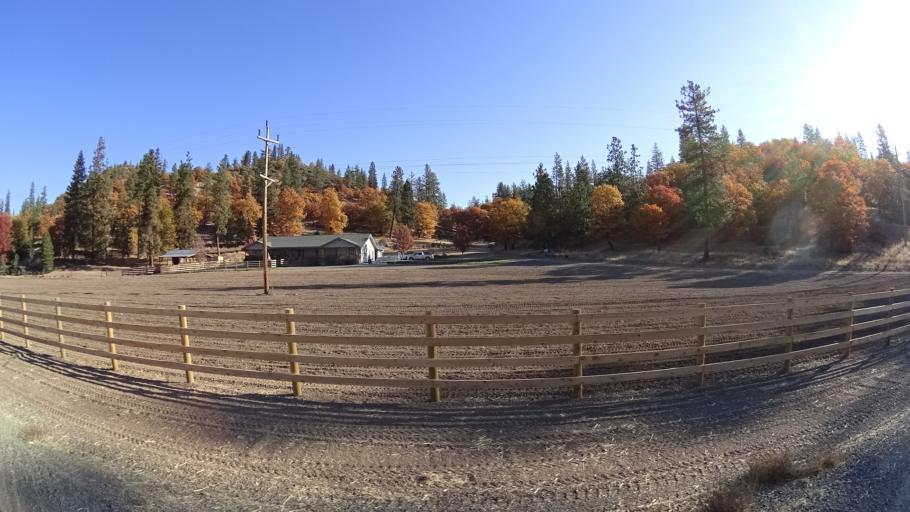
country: US
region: California
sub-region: Siskiyou County
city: Yreka
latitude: 41.6115
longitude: -122.8555
